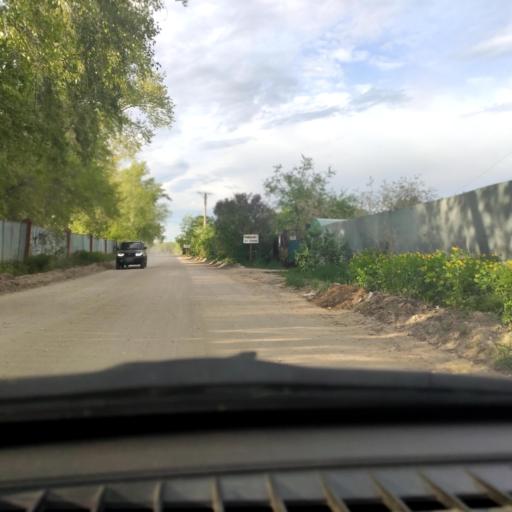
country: RU
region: Samara
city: Zhigulevsk
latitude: 53.4508
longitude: 49.5344
